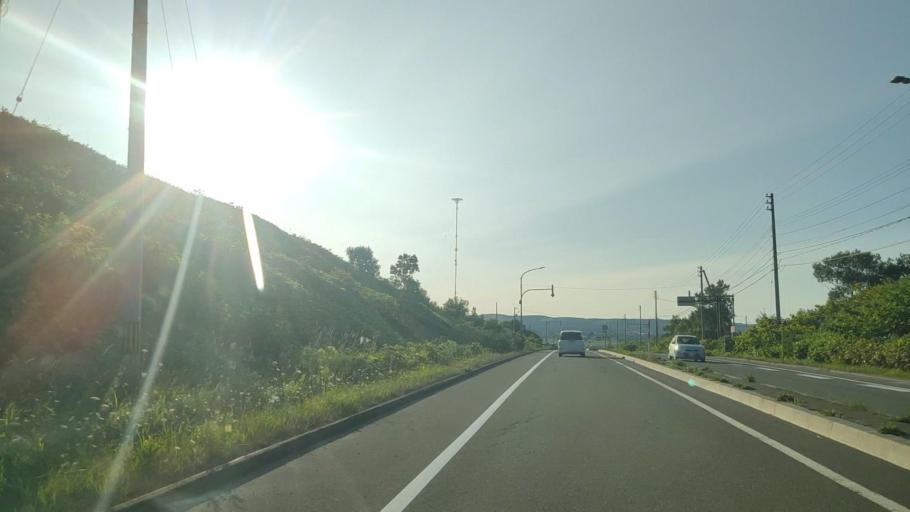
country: JP
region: Hokkaido
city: Wakkanai
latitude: 45.3734
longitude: 141.7170
